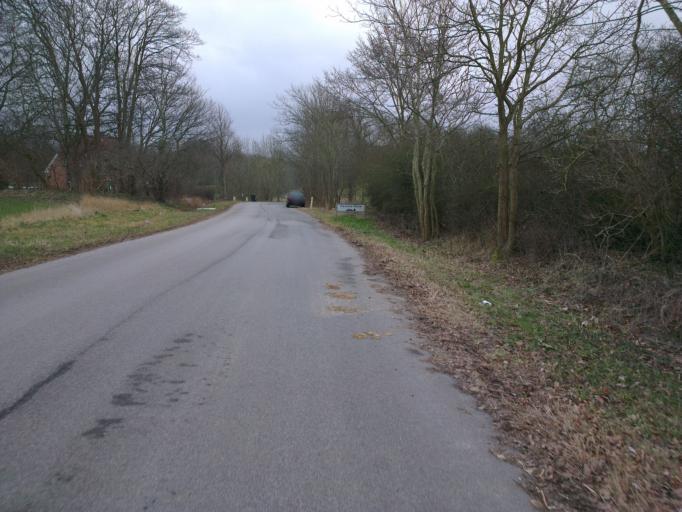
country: DK
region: Capital Region
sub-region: Frederikssund Kommune
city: Frederikssund
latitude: 55.8849
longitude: 12.0660
